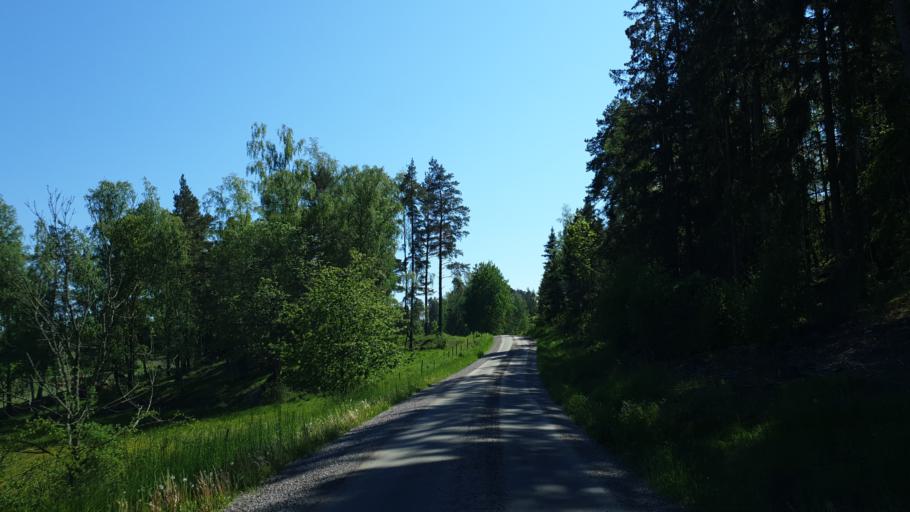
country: SE
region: Soedermanland
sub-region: Trosa Kommun
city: Vagnharad
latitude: 58.9273
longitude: 17.5152
